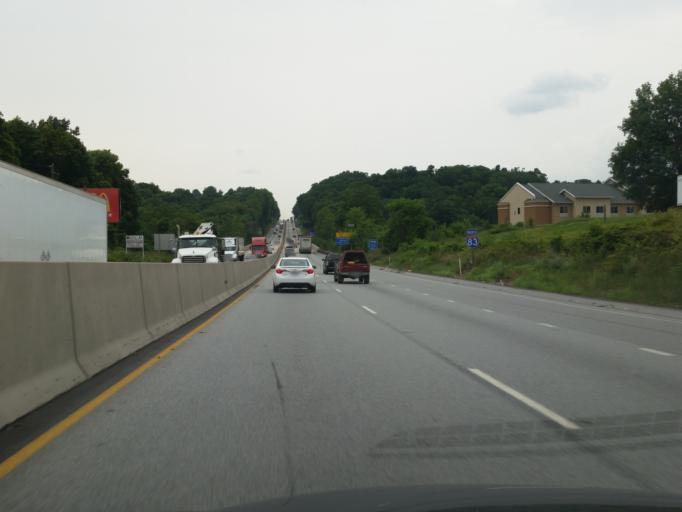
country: US
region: Pennsylvania
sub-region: Cumberland County
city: New Cumberland
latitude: 40.2144
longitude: -76.8808
